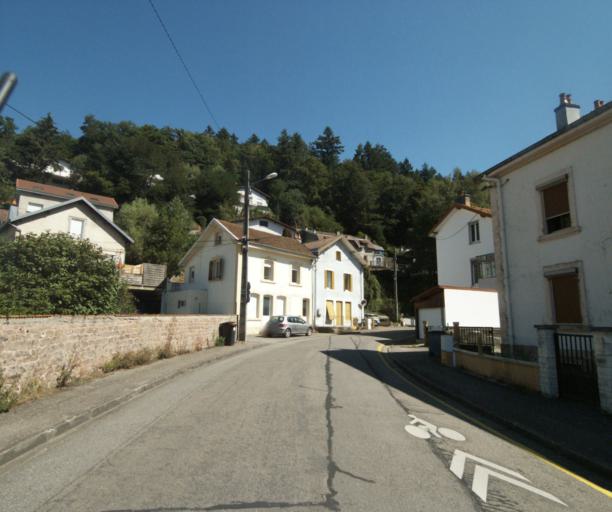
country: FR
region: Lorraine
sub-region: Departement des Vosges
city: Epinal
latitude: 48.1632
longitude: 6.4603
